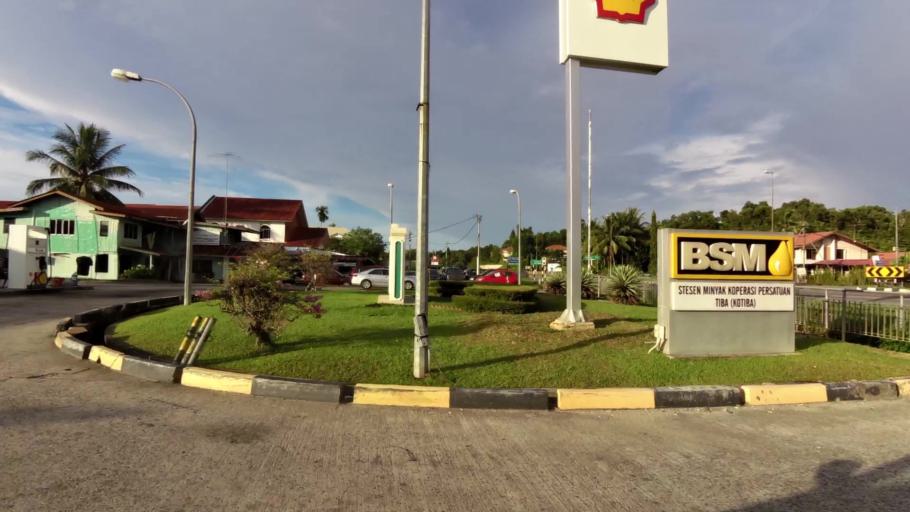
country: BN
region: Brunei and Muara
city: Bandar Seri Begawan
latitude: 4.9785
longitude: 114.9871
